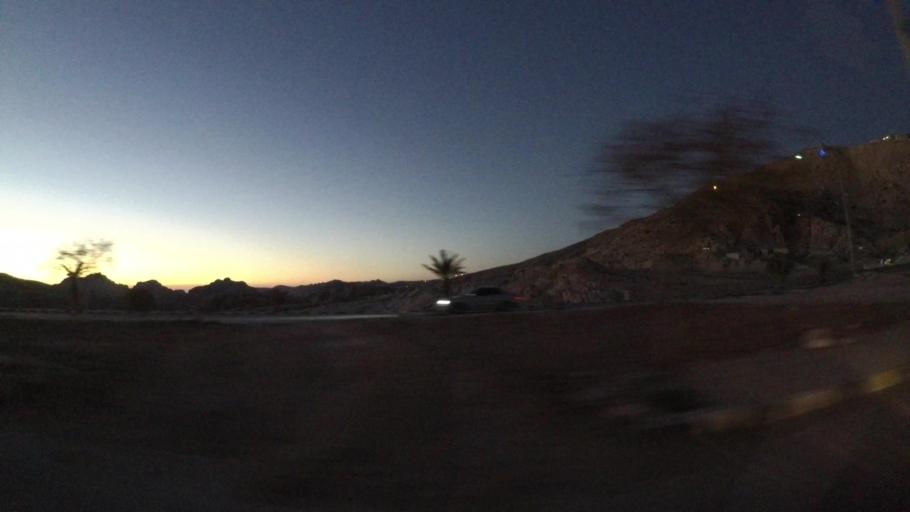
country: JO
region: Ma'an
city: Petra
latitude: 30.3281
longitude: 35.4692
